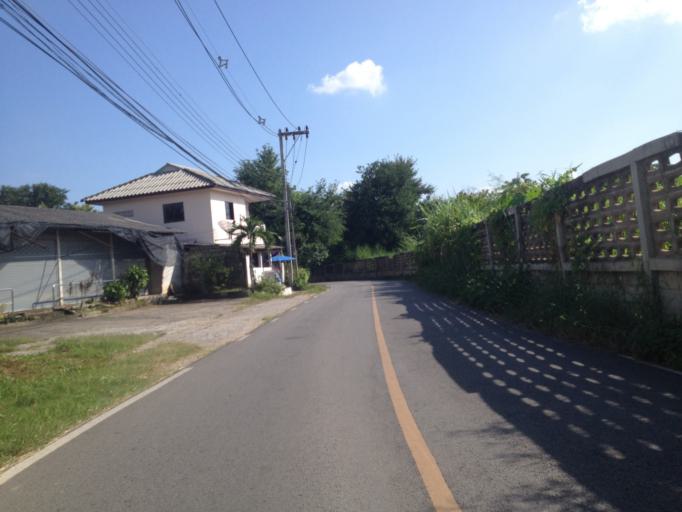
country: TH
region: Chiang Mai
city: Chiang Mai
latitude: 18.7521
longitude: 98.9351
